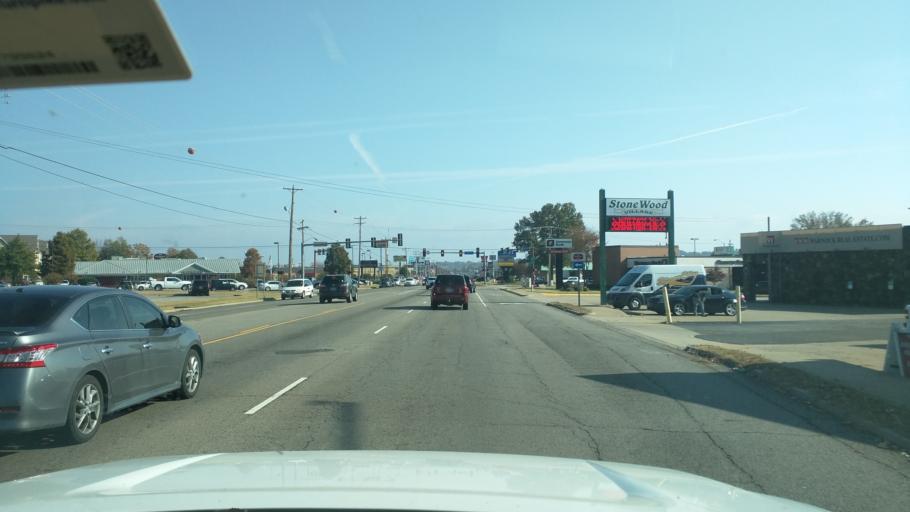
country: US
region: Arkansas
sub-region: Sebastian County
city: Fort Smith
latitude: 35.3533
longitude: -94.3524
